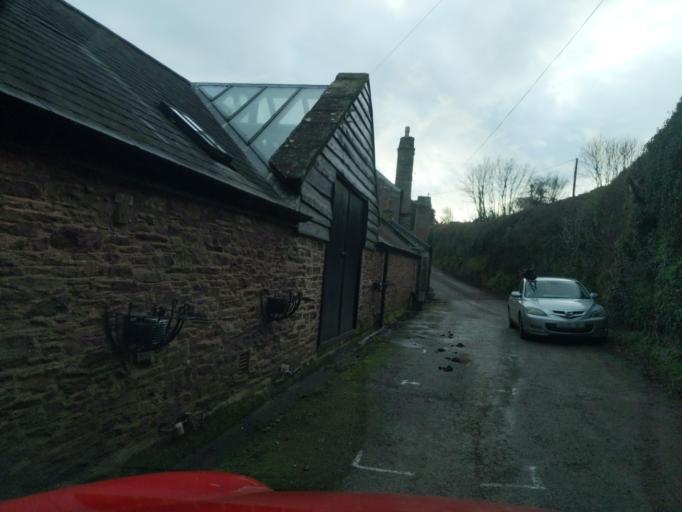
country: GB
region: England
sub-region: Devon
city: Salcombe
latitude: 50.2548
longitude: -3.6699
